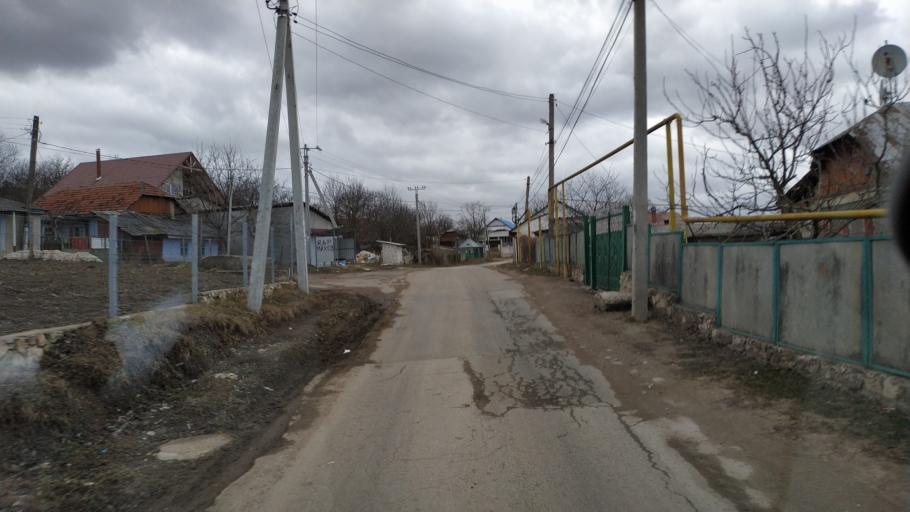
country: MD
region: Calarasi
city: Calarasi
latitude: 47.2428
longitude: 28.3057
